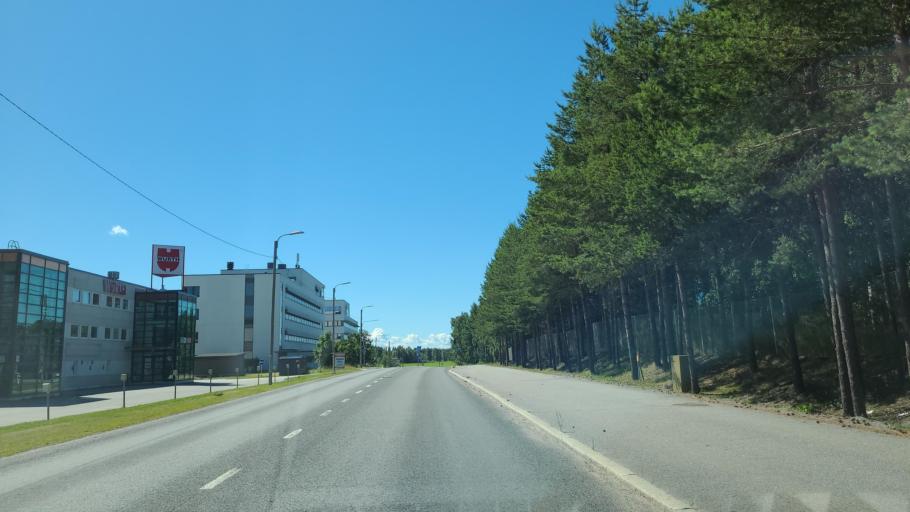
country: FI
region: Ostrobothnia
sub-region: Vaasa
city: Ristinummi
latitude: 63.0586
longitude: 21.7325
